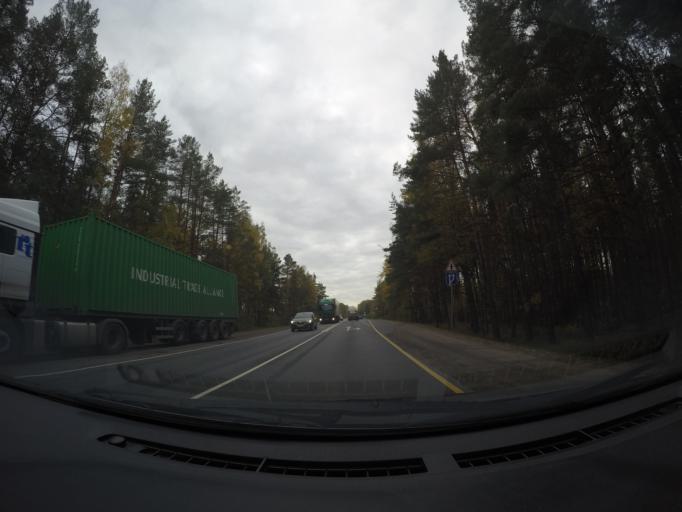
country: RU
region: Moskovskaya
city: Gzhel'
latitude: 55.6471
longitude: 38.3734
